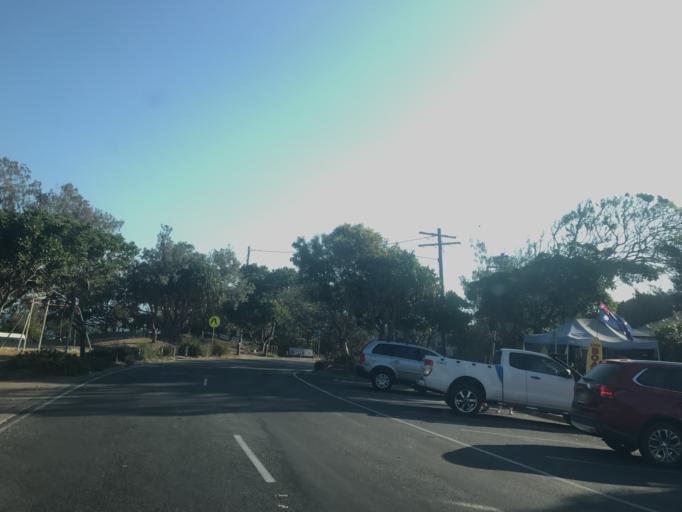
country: AU
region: Queensland
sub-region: Redland
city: Victoria Point
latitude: -27.4338
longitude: 153.5437
